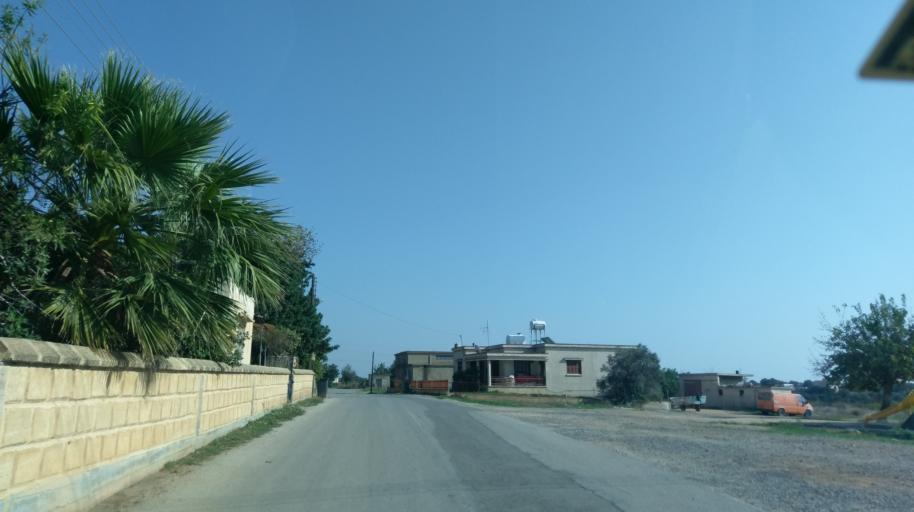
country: CY
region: Ammochostos
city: Leonarisso
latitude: 35.4832
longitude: 34.1883
